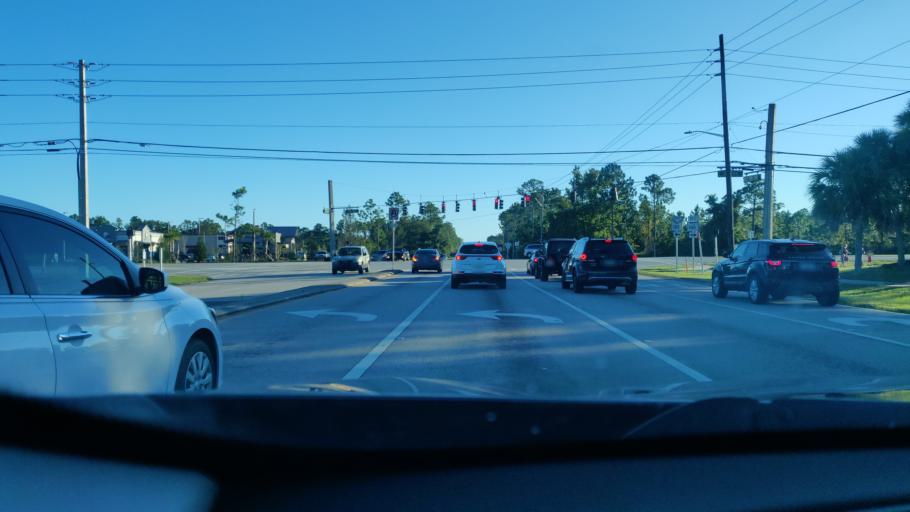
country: US
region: Florida
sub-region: Flagler County
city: Bunnell
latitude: 29.4764
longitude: -81.2216
